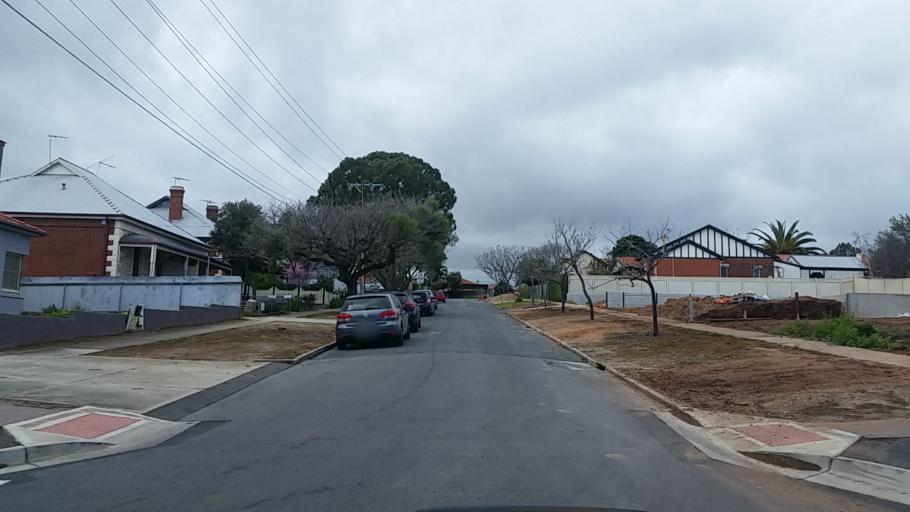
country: AU
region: South Australia
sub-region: Prospect
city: Prospect
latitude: -34.8760
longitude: 138.5918
